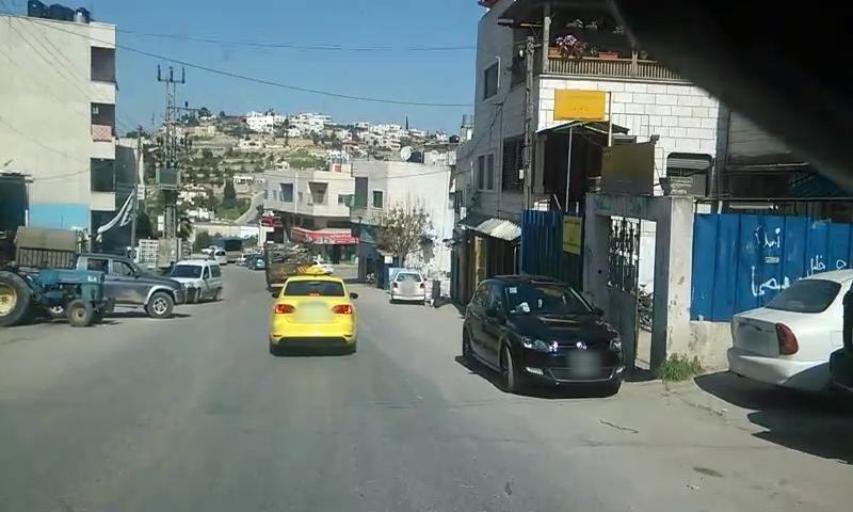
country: PS
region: West Bank
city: Idhna
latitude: 31.5602
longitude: 34.9790
